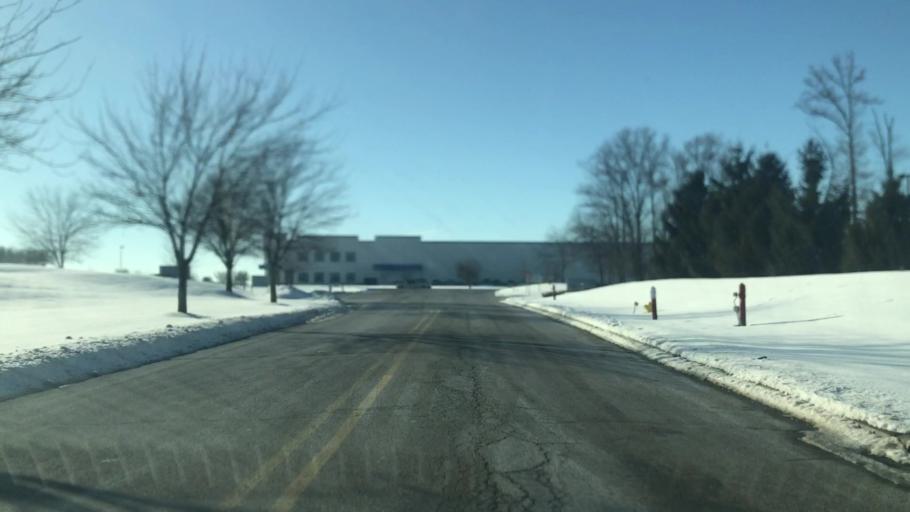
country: US
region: Indiana
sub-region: Hendricks County
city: Plainfield
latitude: 39.6789
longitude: -86.3542
